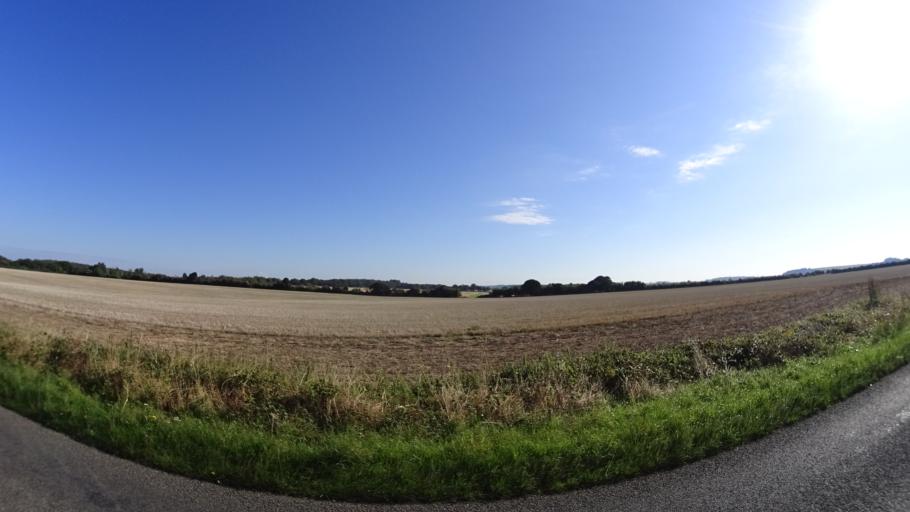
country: GB
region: England
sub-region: Hampshire
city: Abbotts Ann
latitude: 51.1441
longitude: -1.5352
